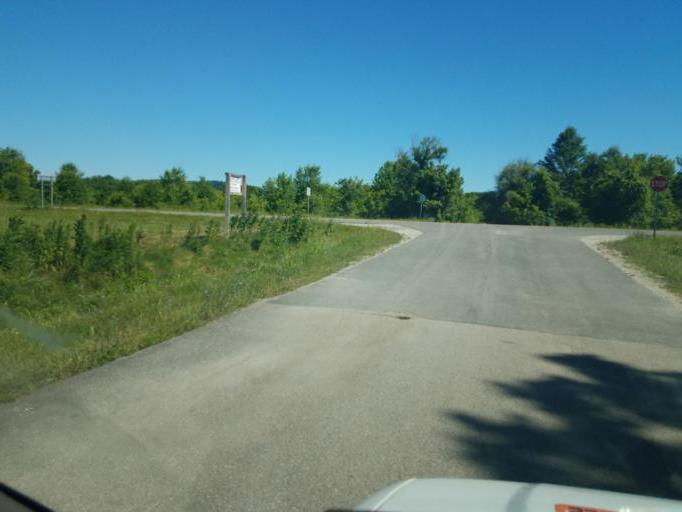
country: US
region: West Virginia
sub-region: Cabell County
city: Lesage
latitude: 38.5849
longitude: -82.2164
